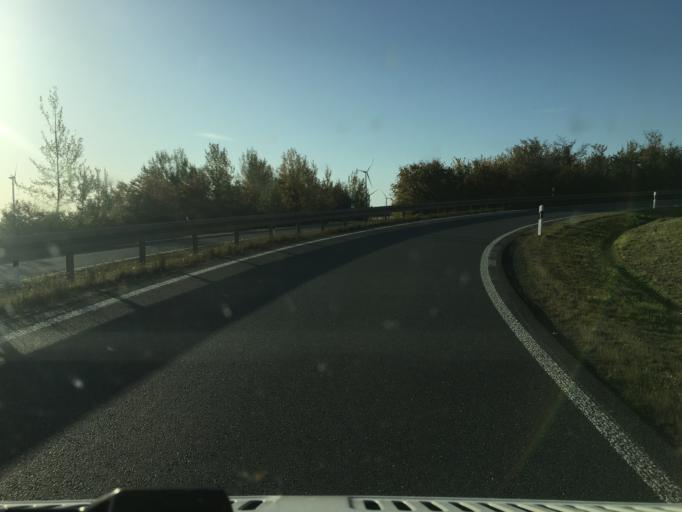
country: DE
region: Thuringia
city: Heyersdorf
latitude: 50.8502
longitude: 12.3378
